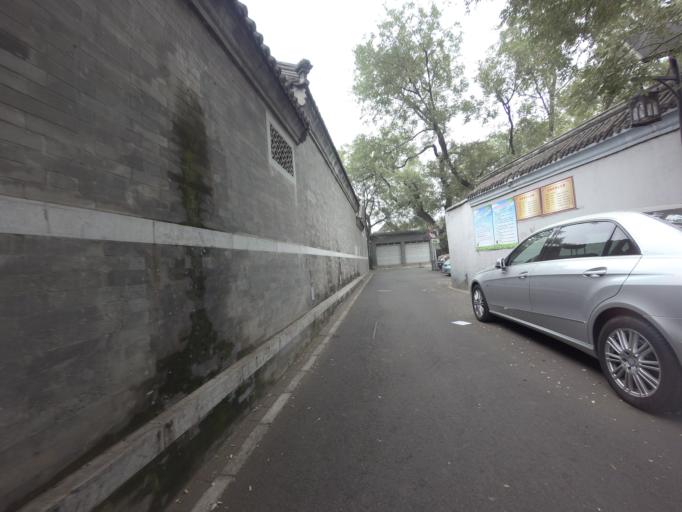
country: CN
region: Beijing
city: Jingshan
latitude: 39.9397
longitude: 116.3835
